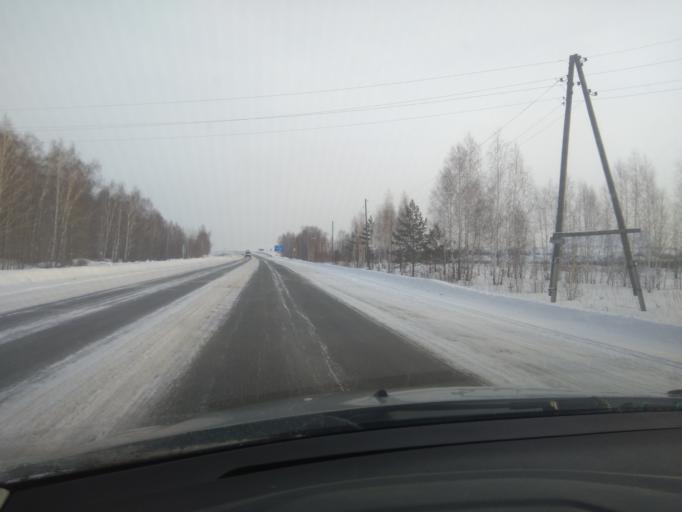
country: RU
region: Sverdlovsk
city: Bogdanovich
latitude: 56.8081
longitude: 62.0348
